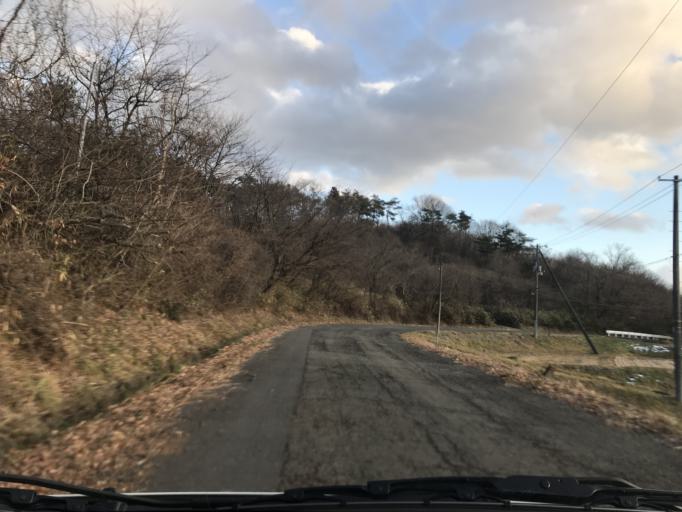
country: JP
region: Iwate
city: Mizusawa
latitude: 39.0354
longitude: 141.1015
